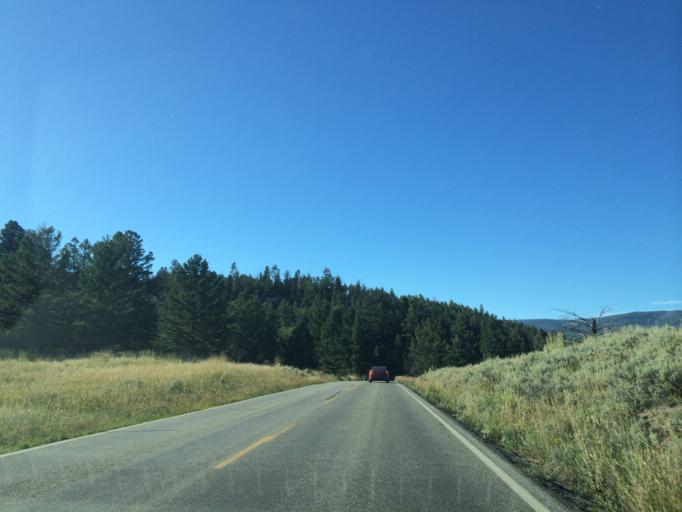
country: US
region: Montana
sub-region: Gallatin County
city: West Yellowstone
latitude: 44.9429
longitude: -110.4500
